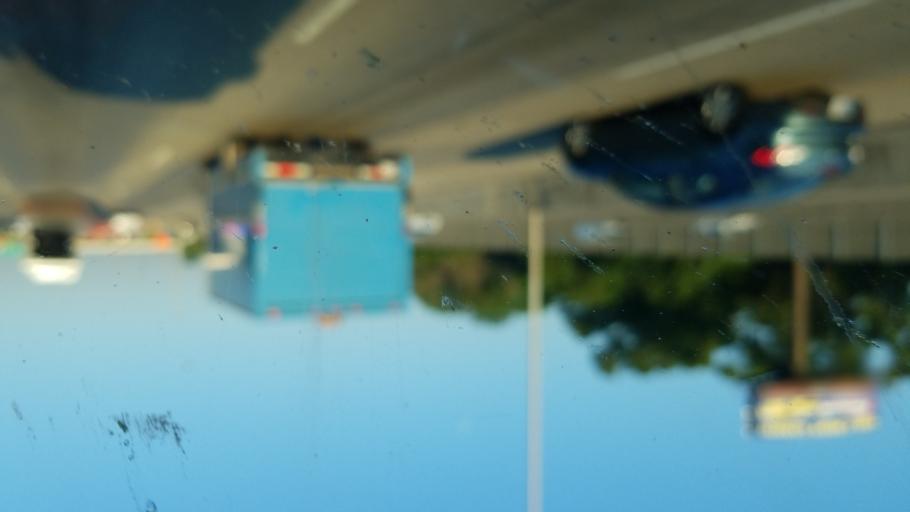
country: US
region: Indiana
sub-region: Lake County
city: New Chicago
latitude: 41.5710
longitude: -87.2916
